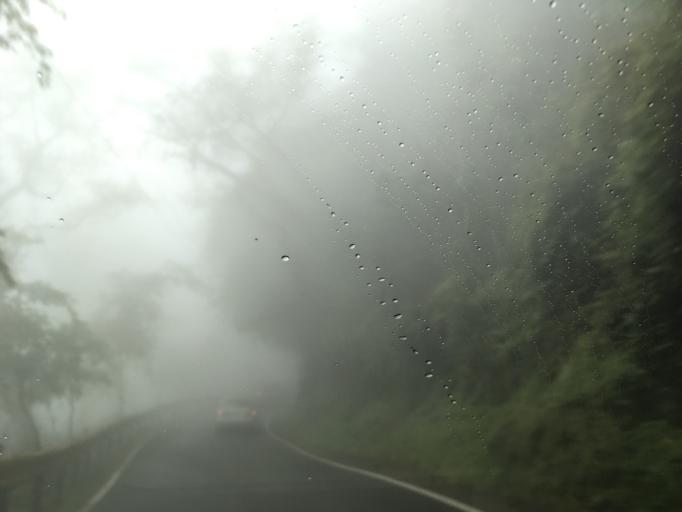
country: TW
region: Taiwan
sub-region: Hualien
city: Hualian
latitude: 24.1882
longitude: 121.4211
